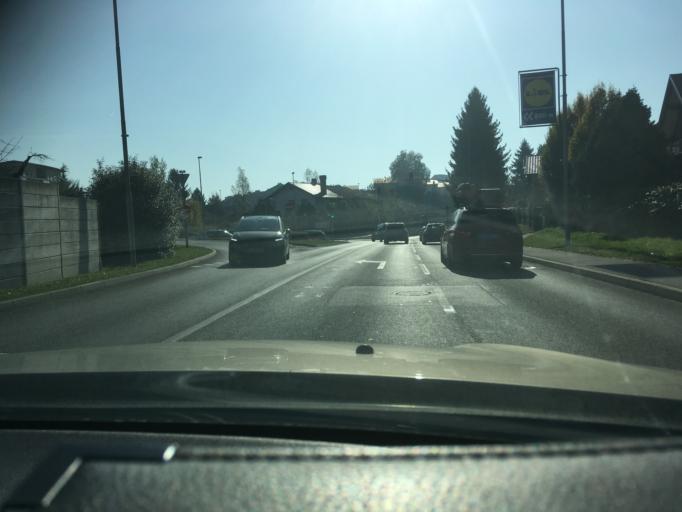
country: SI
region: Domzale
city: Domzale
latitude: 46.1458
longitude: 14.5933
